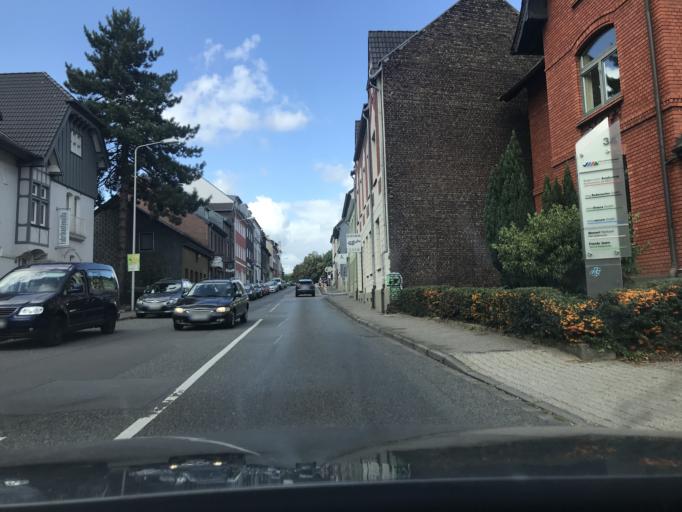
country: DE
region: North Rhine-Westphalia
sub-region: Regierungsbezirk Dusseldorf
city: Erkrath
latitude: 51.2253
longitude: 6.9056
